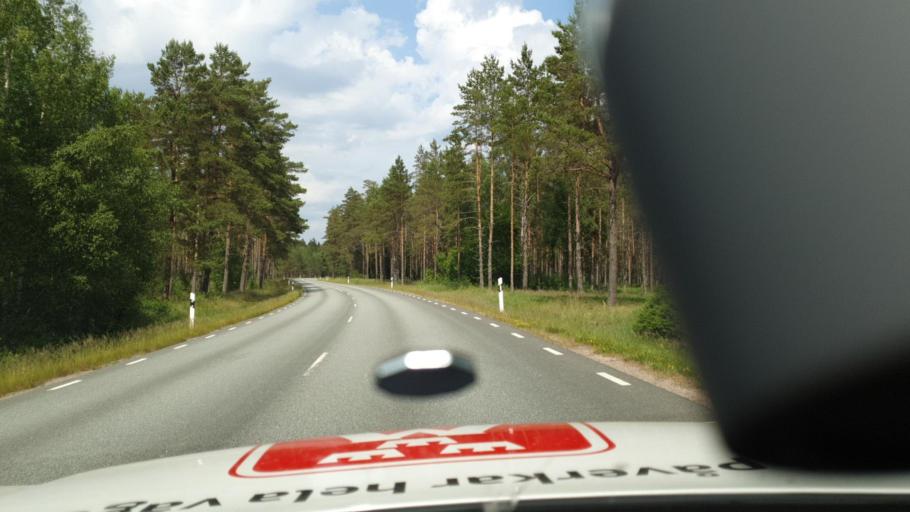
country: SE
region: Joenkoeping
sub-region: Varnamo Kommun
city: Varnamo
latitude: 57.2804
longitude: 14.0639
